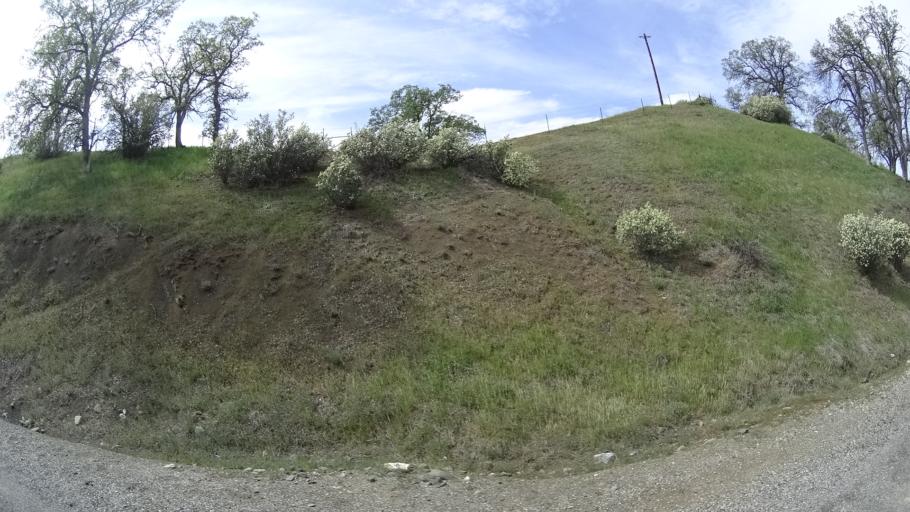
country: US
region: California
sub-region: Glenn County
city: Willows
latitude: 39.6063
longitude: -122.5586
